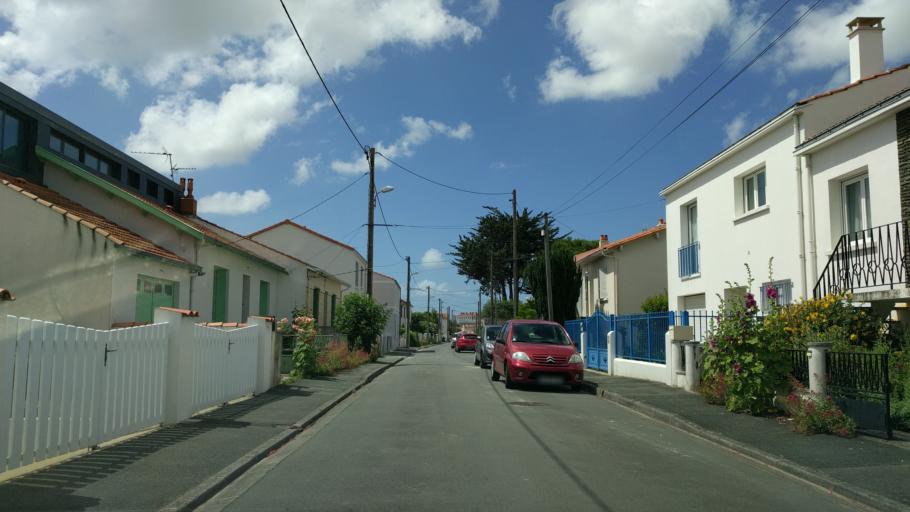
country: FR
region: Poitou-Charentes
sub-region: Departement de la Charente-Maritime
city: La Rochelle
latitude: 46.1737
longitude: -1.1420
